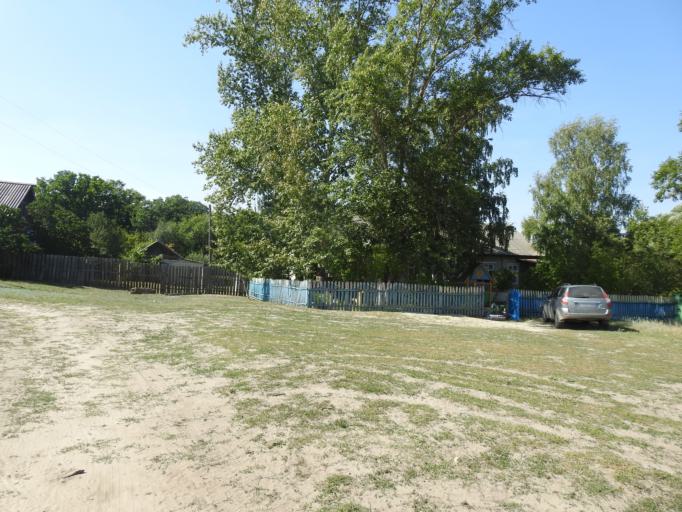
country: RU
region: Saratov
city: Lysyye Gory
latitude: 51.3104
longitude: 45.0064
